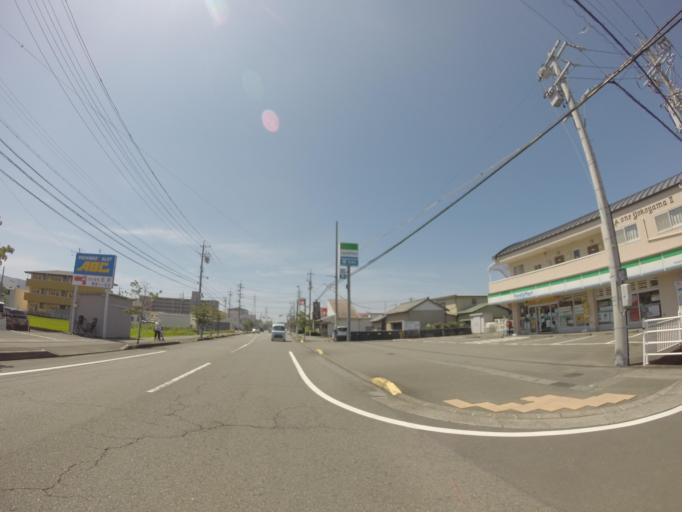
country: JP
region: Shizuoka
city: Fujieda
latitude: 34.8541
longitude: 138.2889
